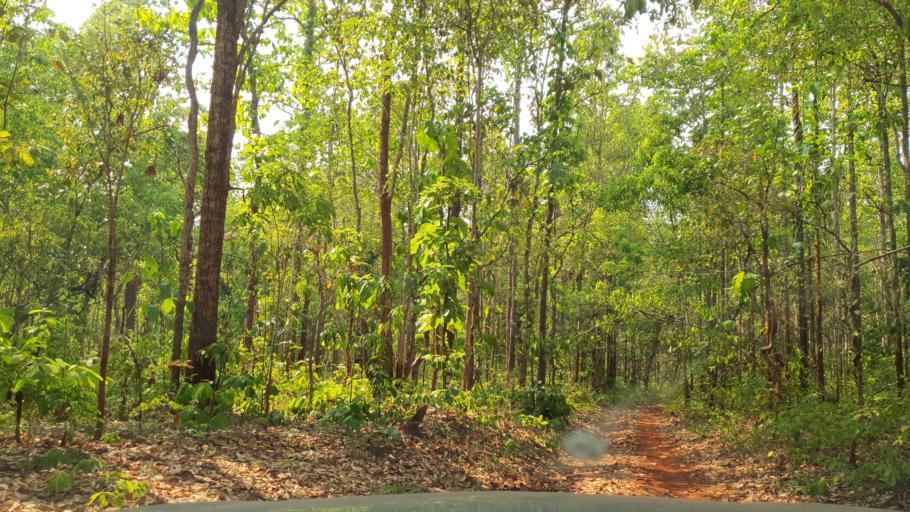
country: TH
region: Chiang Mai
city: San Sai
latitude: 19.0072
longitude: 99.1169
